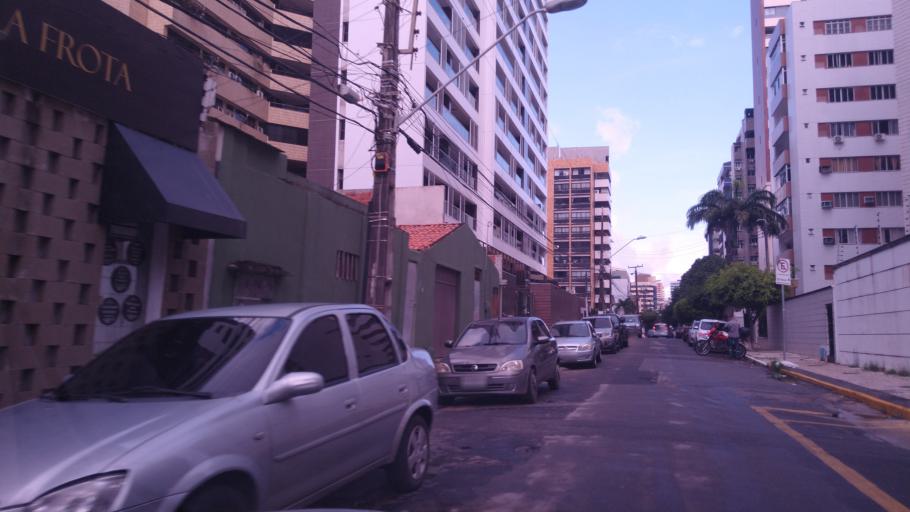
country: BR
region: Ceara
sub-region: Fortaleza
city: Fortaleza
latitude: -3.7273
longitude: -38.4893
